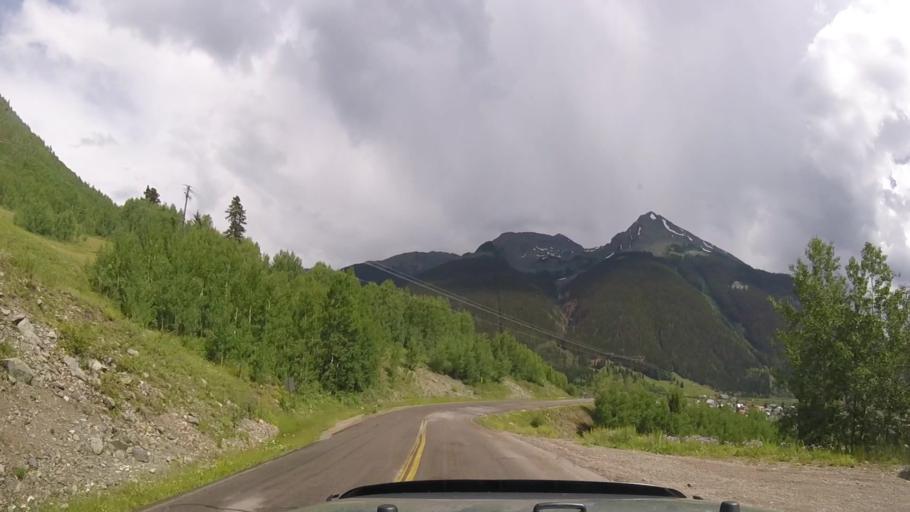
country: US
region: Colorado
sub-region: San Juan County
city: Silverton
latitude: 37.8204
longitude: -107.6614
